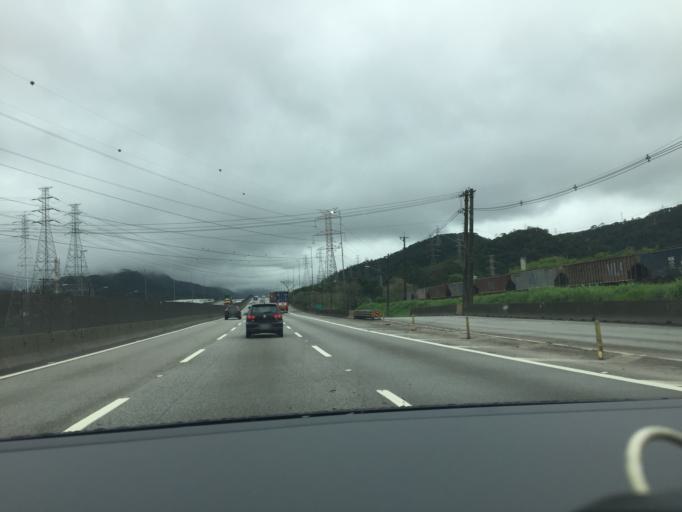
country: BR
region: Sao Paulo
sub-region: Cubatao
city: Cubatao
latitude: -23.8697
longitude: -46.4204
